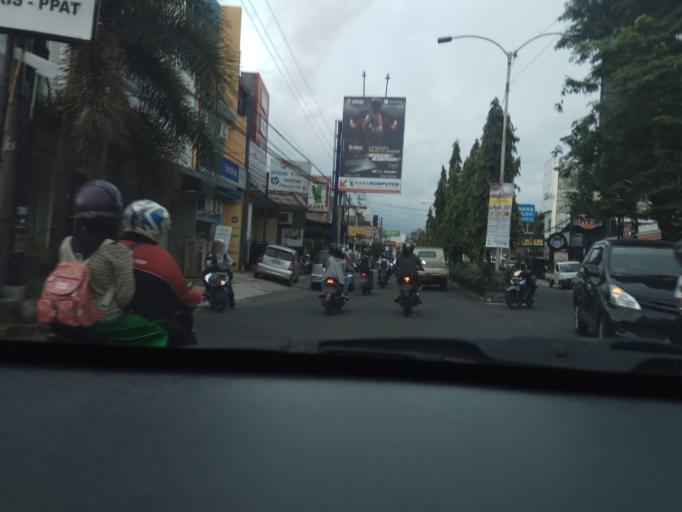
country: ID
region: Daerah Istimewa Yogyakarta
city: Yogyakarta
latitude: -7.7651
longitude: 110.3924
